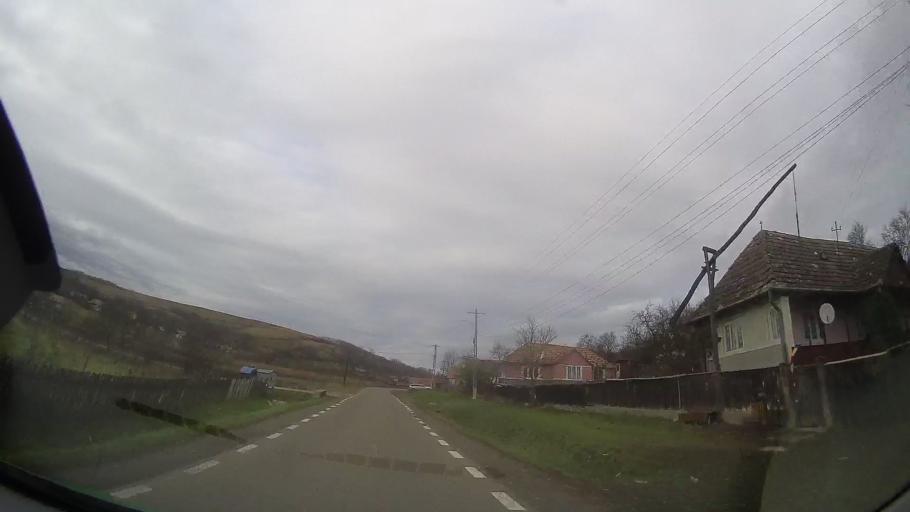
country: RO
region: Mures
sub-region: Comuna Cozma
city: Cozma
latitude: 46.8038
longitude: 24.5304
